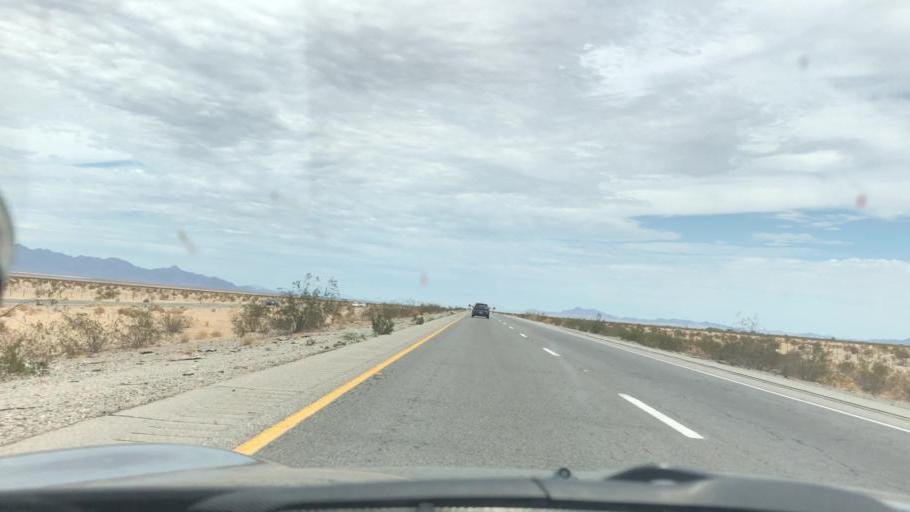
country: US
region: California
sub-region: Riverside County
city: Mesa Verde
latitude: 33.6397
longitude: -115.0975
